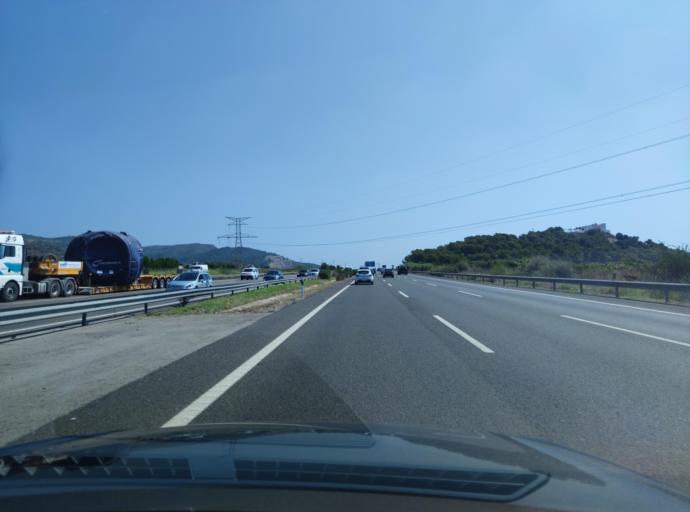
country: ES
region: Valencia
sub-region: Provincia de Valencia
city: Petres
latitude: 39.6867
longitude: -0.2919
